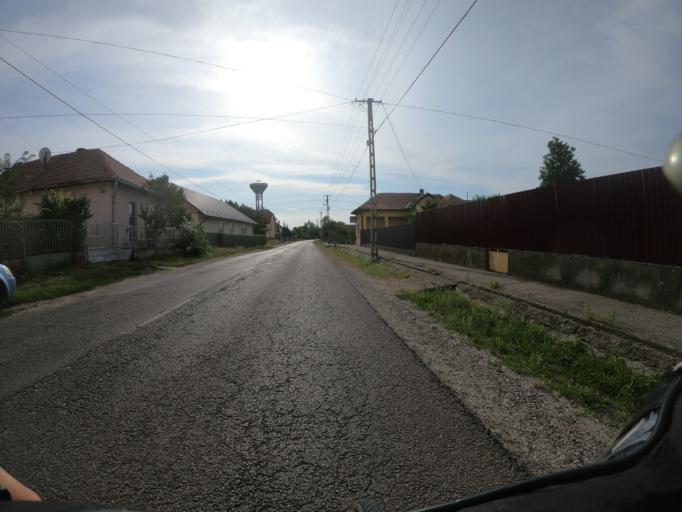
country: HU
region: Borsod-Abauj-Zemplen
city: Mezocsat
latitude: 47.8207
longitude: 20.9131
